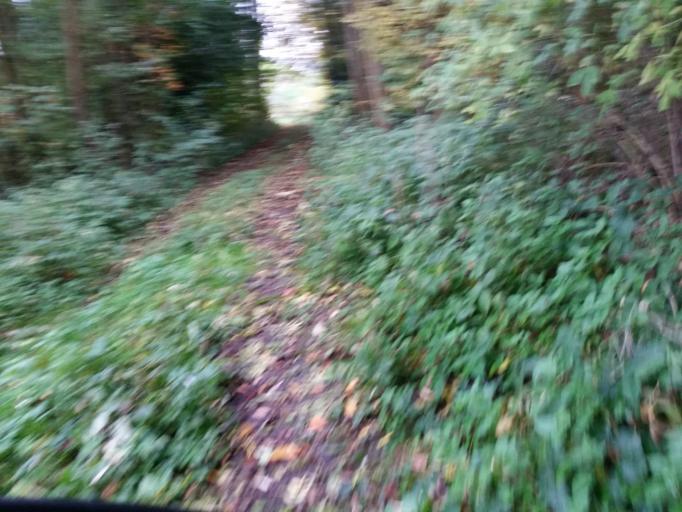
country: BE
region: Flanders
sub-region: Provincie Vlaams-Brabant
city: Zemst
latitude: 50.9887
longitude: 4.4766
